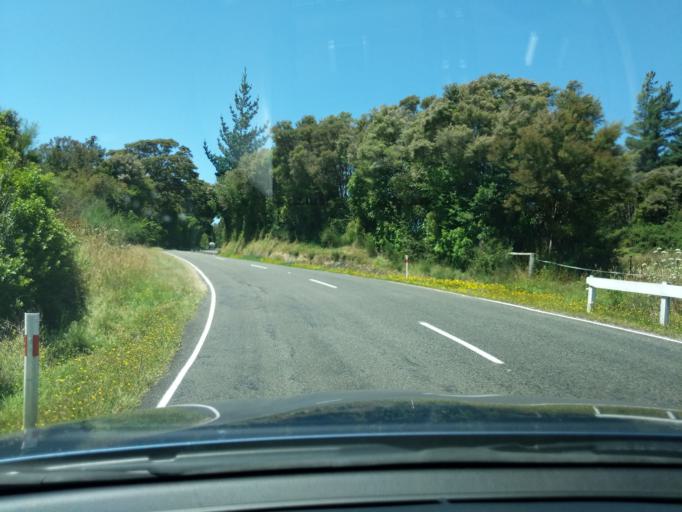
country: NZ
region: Tasman
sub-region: Tasman District
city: Takaka
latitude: -40.7253
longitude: 172.5948
